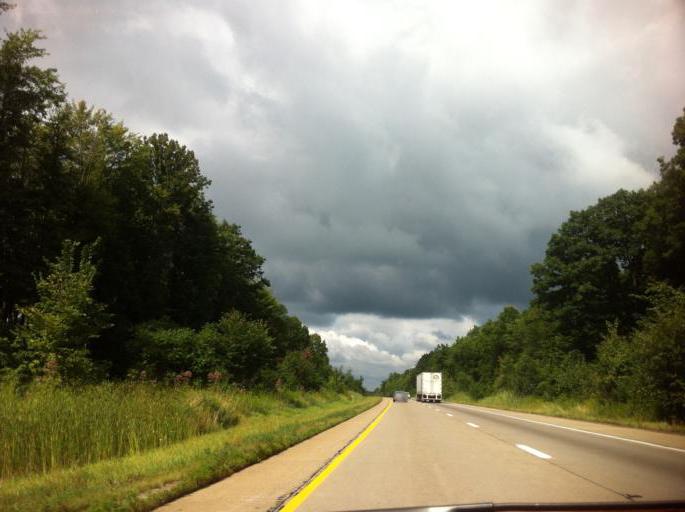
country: US
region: Pennsylvania
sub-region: Lawrence County
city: New Wilmington
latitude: 41.1864
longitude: -80.3491
